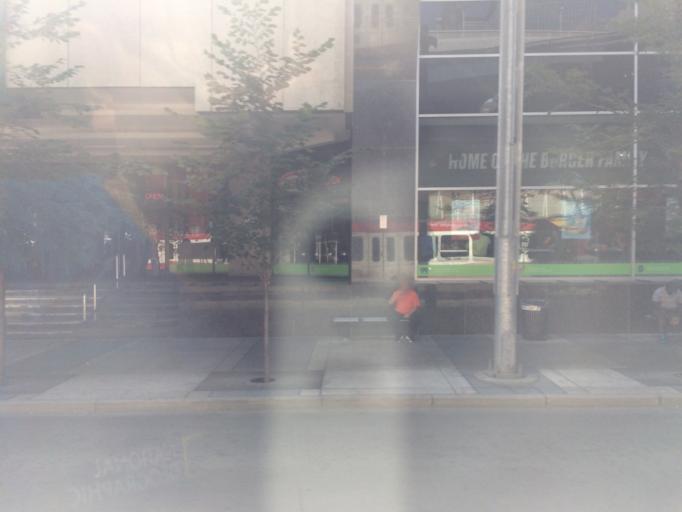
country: CA
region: Alberta
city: Calgary
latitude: 51.0467
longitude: -114.0670
